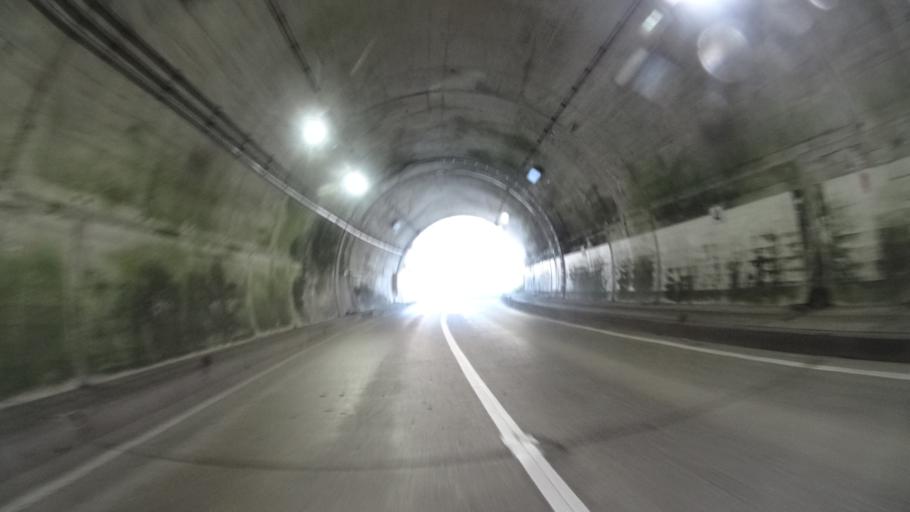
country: JP
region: Ishikawa
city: Tsurugi-asahimachi
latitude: 36.3613
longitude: 136.6083
